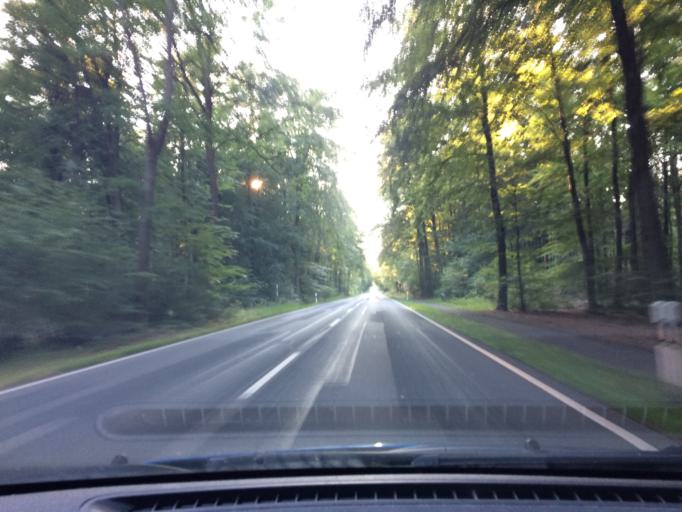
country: DE
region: Lower Saxony
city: Unterluss
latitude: 52.8189
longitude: 10.3359
